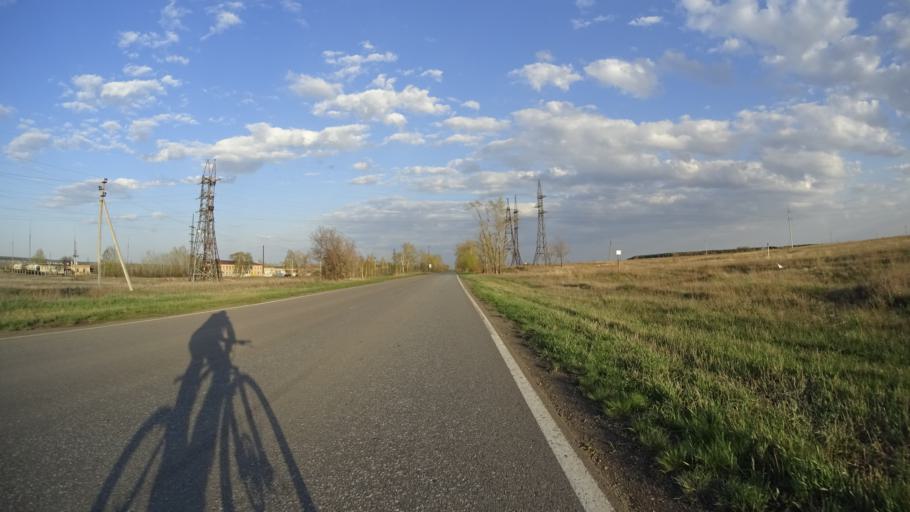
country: RU
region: Chelyabinsk
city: Troitsk
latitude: 54.0574
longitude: 61.5835
